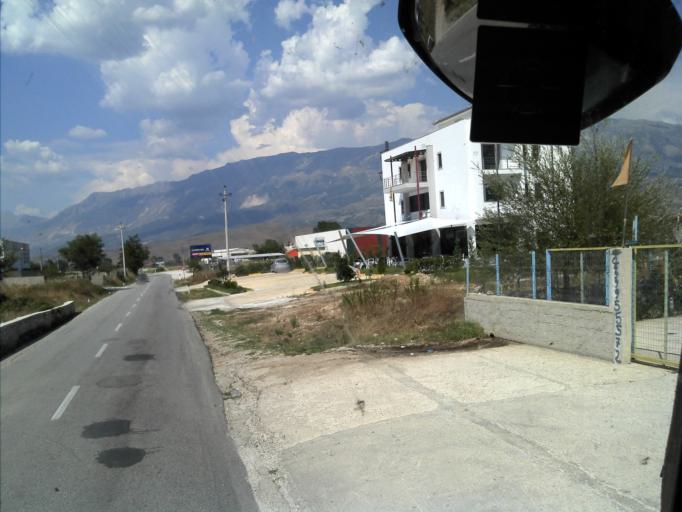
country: AL
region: Gjirokaster
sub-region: Rrethi i Gjirokastres
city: Dervician
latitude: 40.0498
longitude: 20.1772
